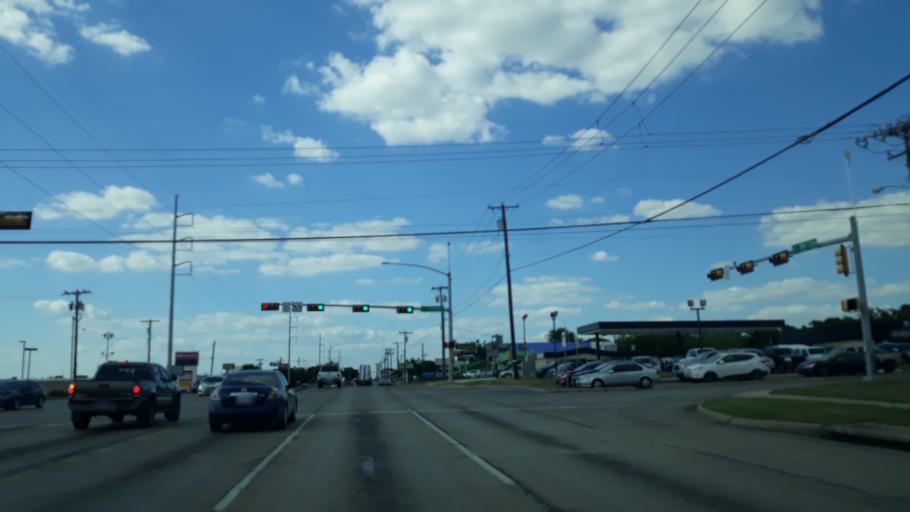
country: US
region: Texas
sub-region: Dallas County
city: Irving
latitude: 32.8282
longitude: -96.9937
